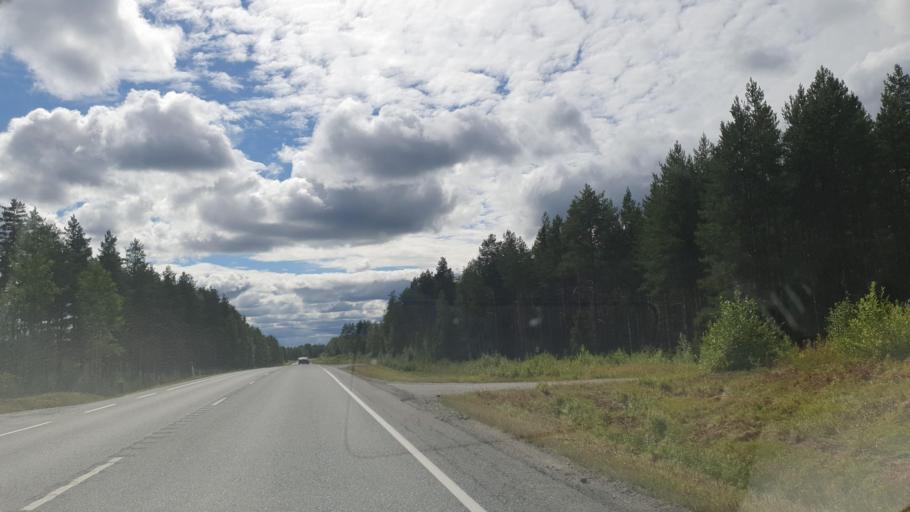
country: FI
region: Kainuu
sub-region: Kajaani
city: Kajaani
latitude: 64.1286
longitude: 27.4756
